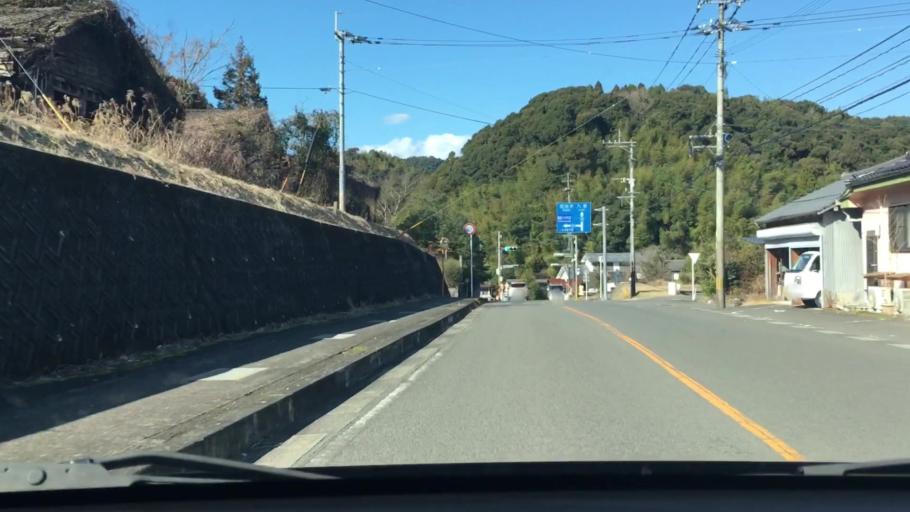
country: JP
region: Kagoshima
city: Satsumasendai
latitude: 31.7781
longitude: 130.4004
